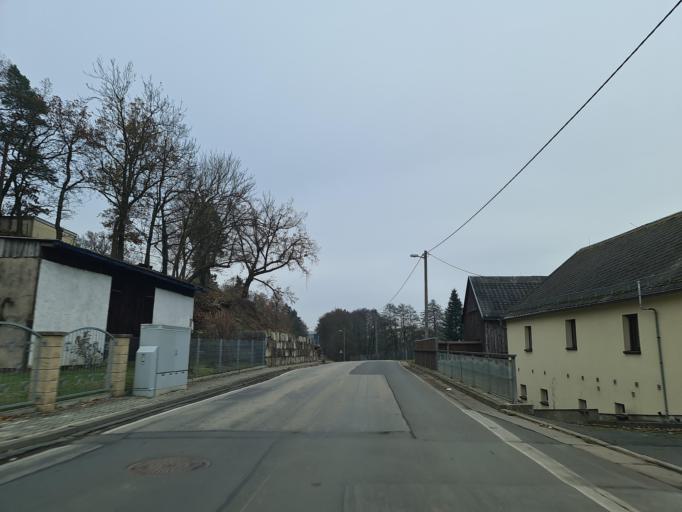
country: DE
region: Saxony
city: Syrau
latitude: 50.5114
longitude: 12.0915
